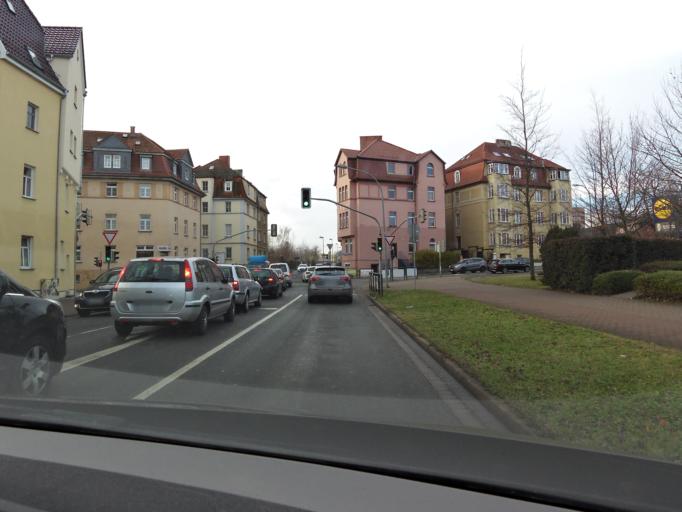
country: DE
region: Thuringia
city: Weimar
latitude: 50.9937
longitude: 11.3210
